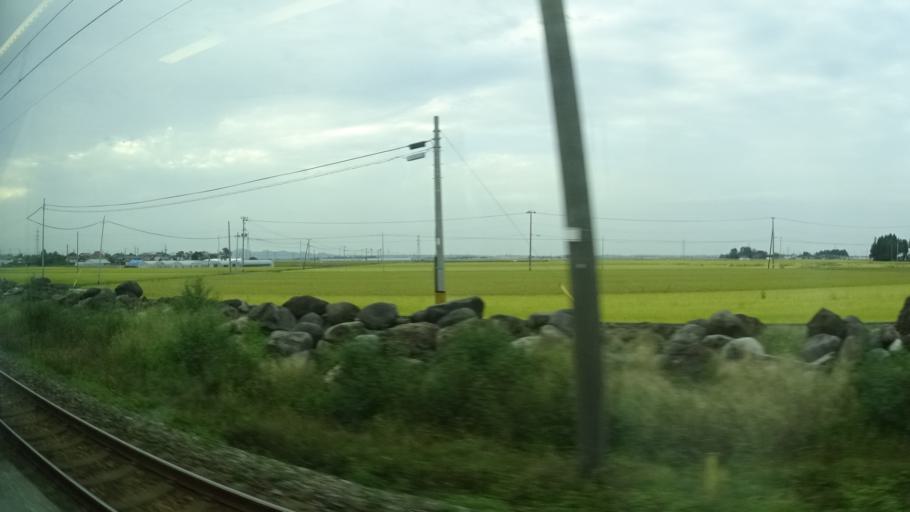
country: JP
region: Yamagata
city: Tsuruoka
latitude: 38.7718
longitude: 139.8978
